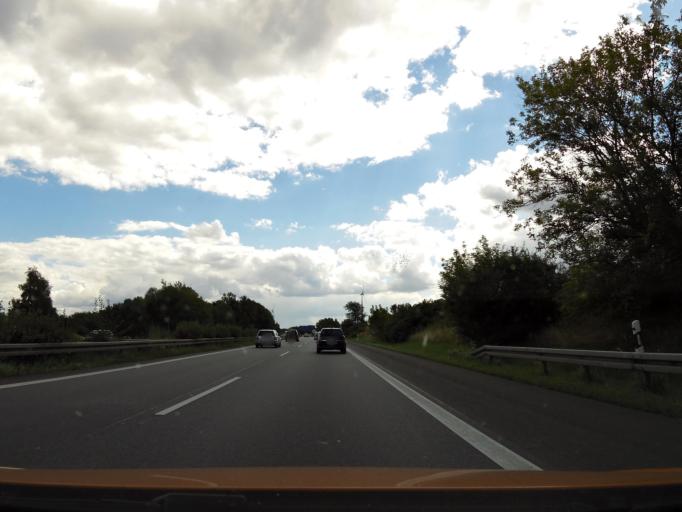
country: DE
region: Berlin
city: Blankenfelde
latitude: 52.6503
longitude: 13.4180
